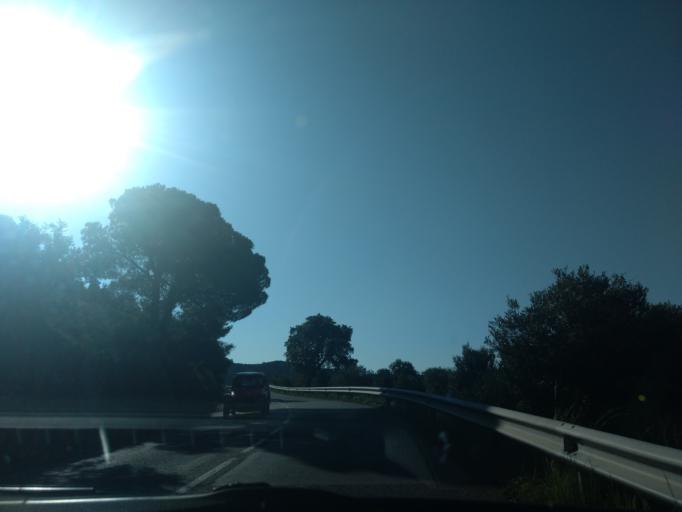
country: ES
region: Catalonia
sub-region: Provincia de Girona
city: Roses
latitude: 42.2955
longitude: 3.1926
